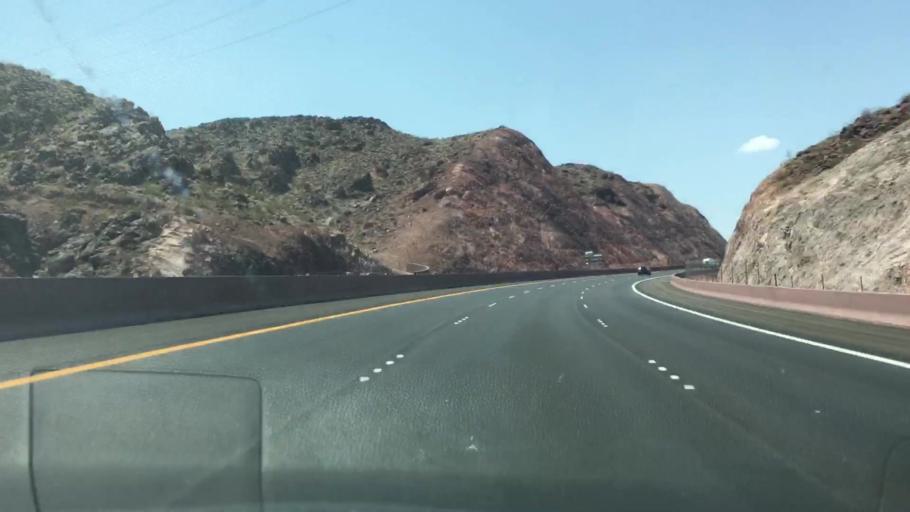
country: US
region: Nevada
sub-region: Clark County
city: Boulder City
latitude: 36.0036
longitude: -114.7850
